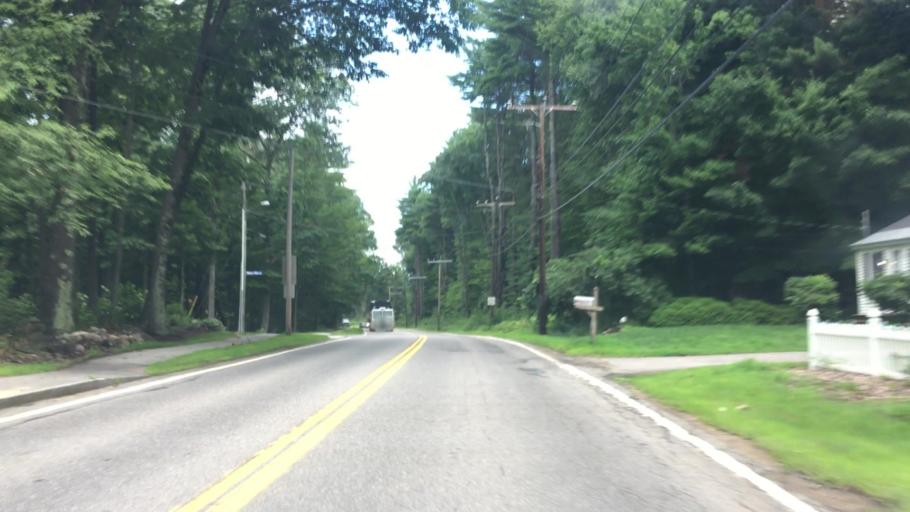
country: US
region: New Hampshire
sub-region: Belknap County
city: Laconia
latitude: 43.5591
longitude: -71.4726
